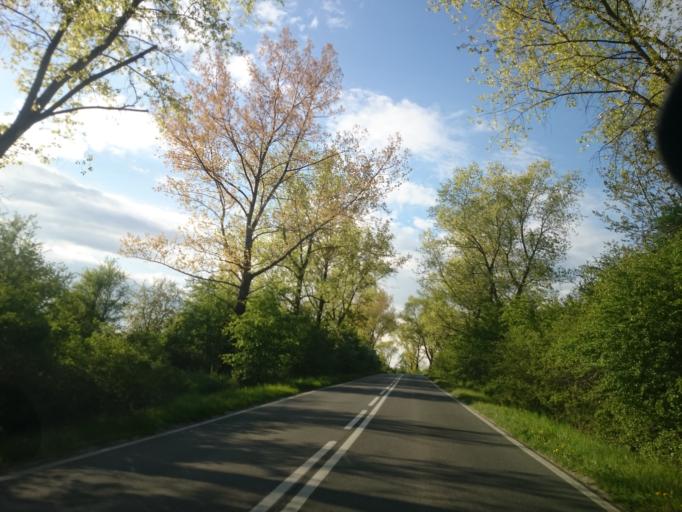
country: PL
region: Lower Silesian Voivodeship
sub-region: Powiat zabkowicki
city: Kamieniec Zabkowicki
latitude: 50.5489
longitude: 16.8597
